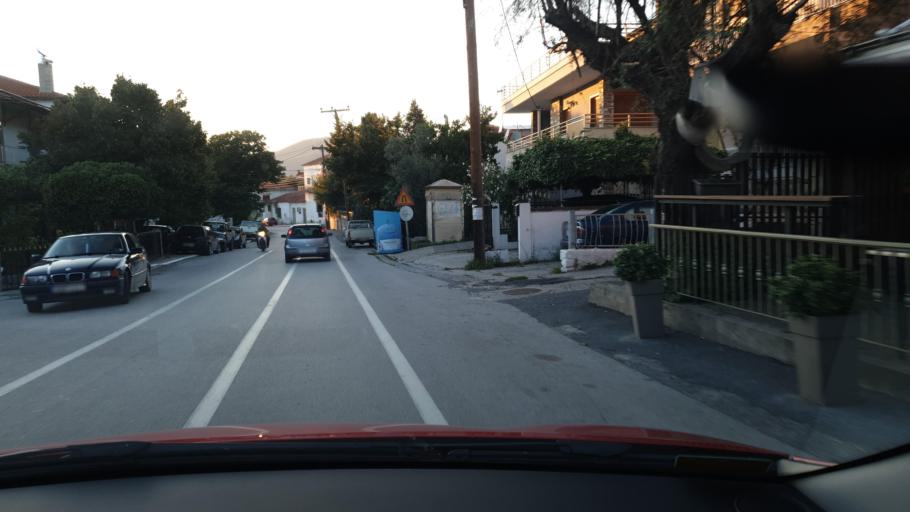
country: GR
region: Central Macedonia
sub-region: Nomos Chalkidikis
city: Galatista
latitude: 40.4670
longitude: 23.2785
